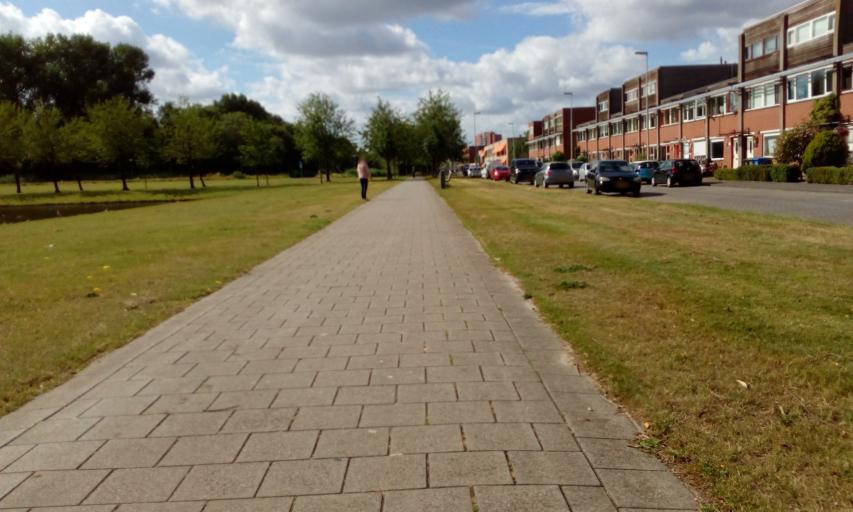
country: NL
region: South Holland
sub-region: Gemeente Rotterdam
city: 's-Gravenland
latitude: 51.9368
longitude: 4.5443
